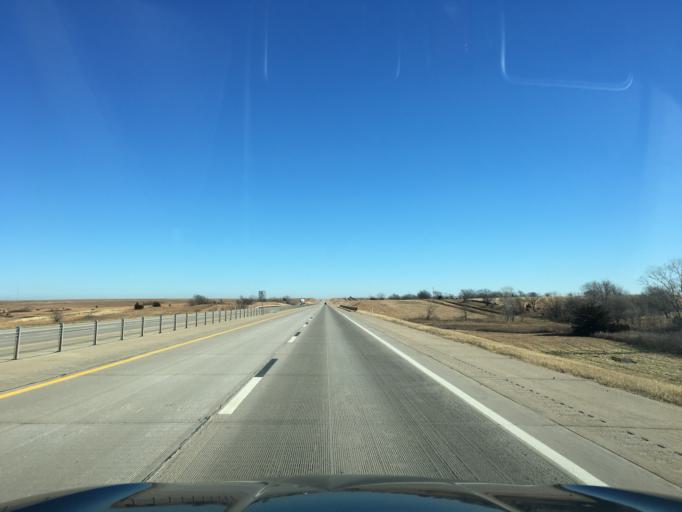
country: US
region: Oklahoma
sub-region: Noble County
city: Perry
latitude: 36.3920
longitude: -97.1739
